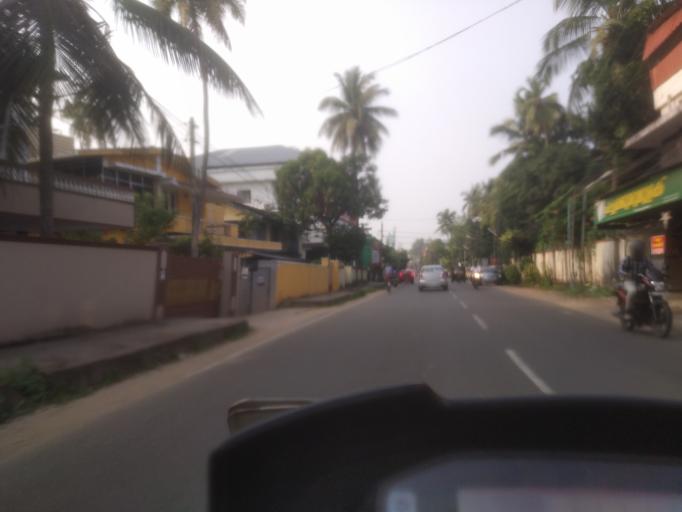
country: IN
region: Kerala
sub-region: Alappuzha
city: Arukutti
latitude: 9.9398
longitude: 76.3473
